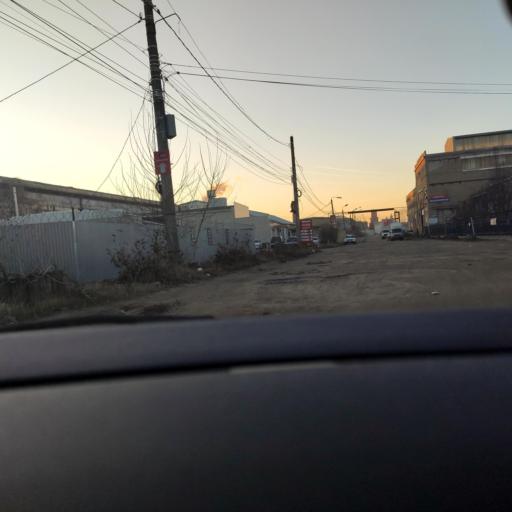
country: RU
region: Voronezj
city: Voronezh
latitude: 51.6882
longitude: 39.1799
